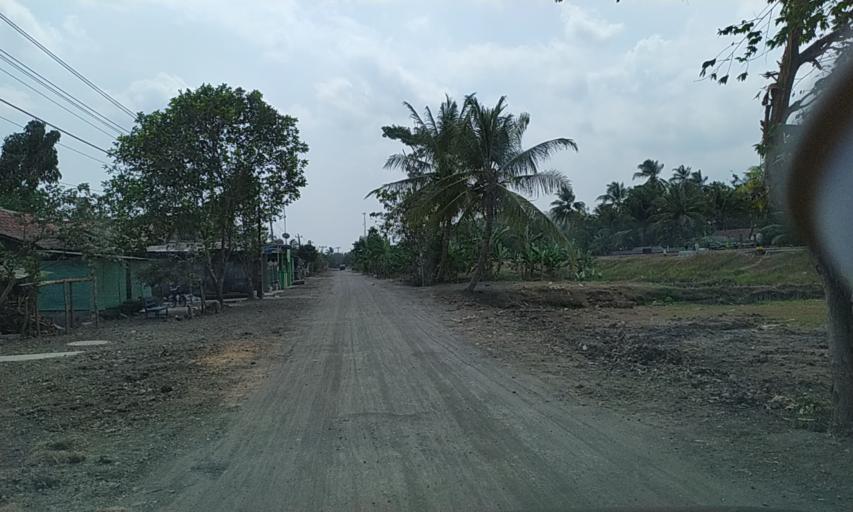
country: ID
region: Central Java
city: Karangtengah
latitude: -7.4425
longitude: 108.7648
